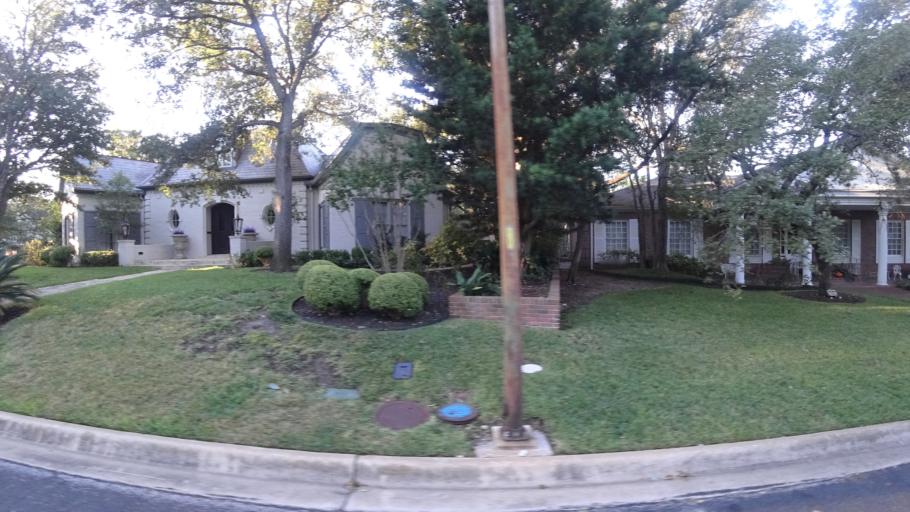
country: US
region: Texas
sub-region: Travis County
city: West Lake Hills
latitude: 30.3030
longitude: -97.7781
